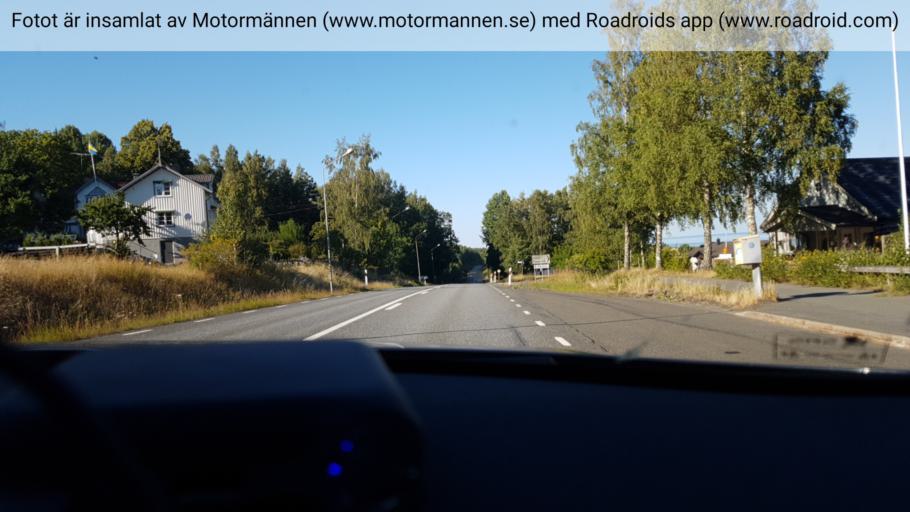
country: SE
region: Joenkoeping
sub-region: Habo Kommun
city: Habo
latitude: 58.0167
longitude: 14.1445
